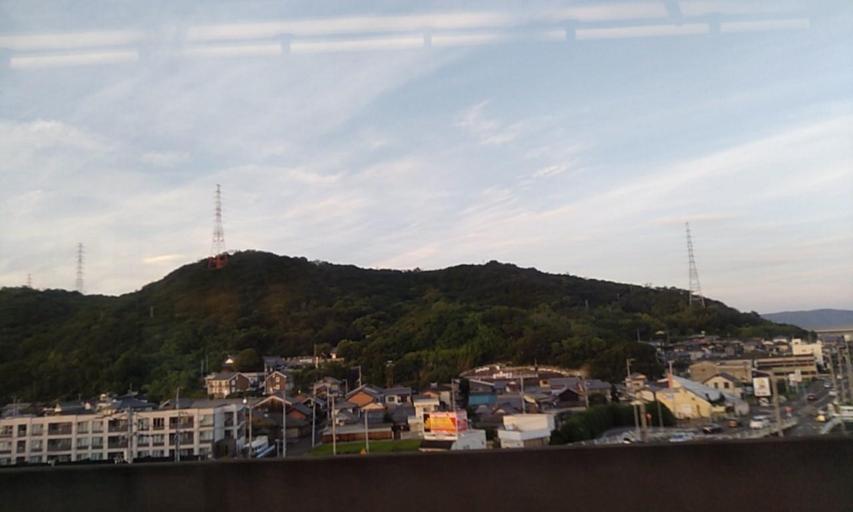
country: JP
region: Kagawa
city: Sakaidecho
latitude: 34.3117
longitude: 133.8320
